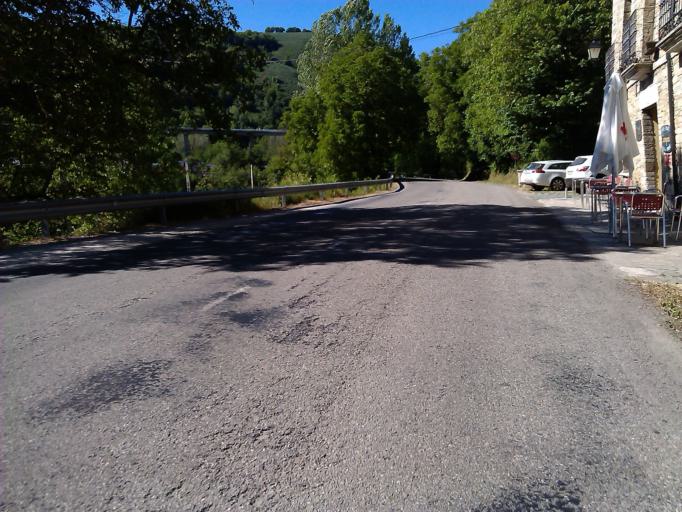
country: ES
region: Castille and Leon
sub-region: Provincia de Leon
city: Vega de Valcarce
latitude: 42.6635
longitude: -6.9267
